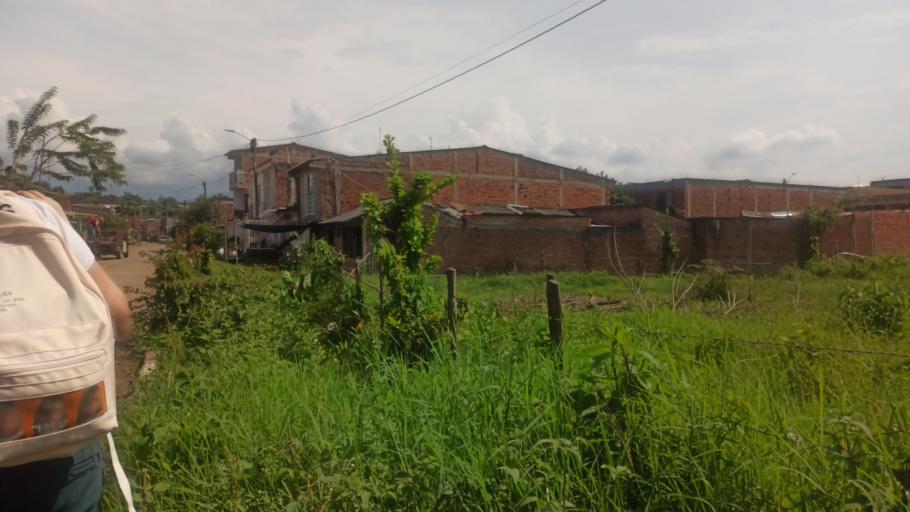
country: CO
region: Cauca
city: Buenos Aires
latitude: 3.1255
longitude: -76.5915
